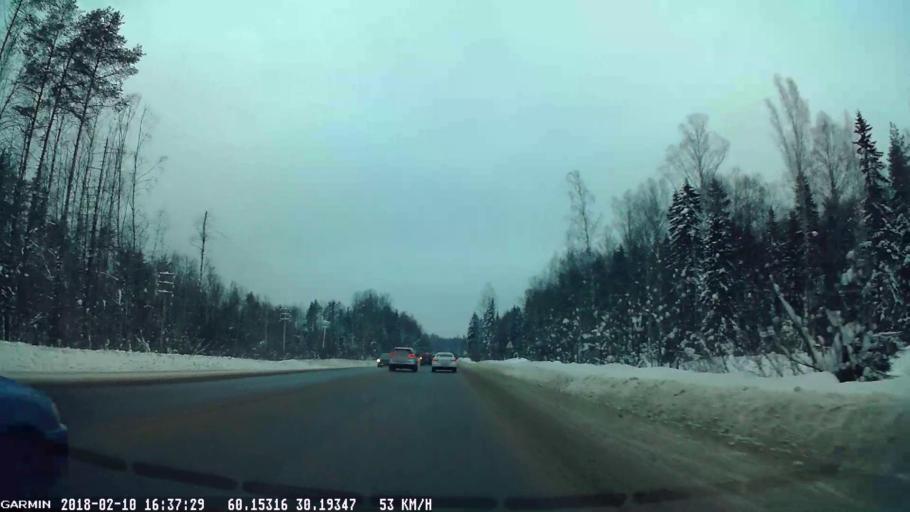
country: RU
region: Leningrad
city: Sertolovo
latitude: 60.1504
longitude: 30.1970
